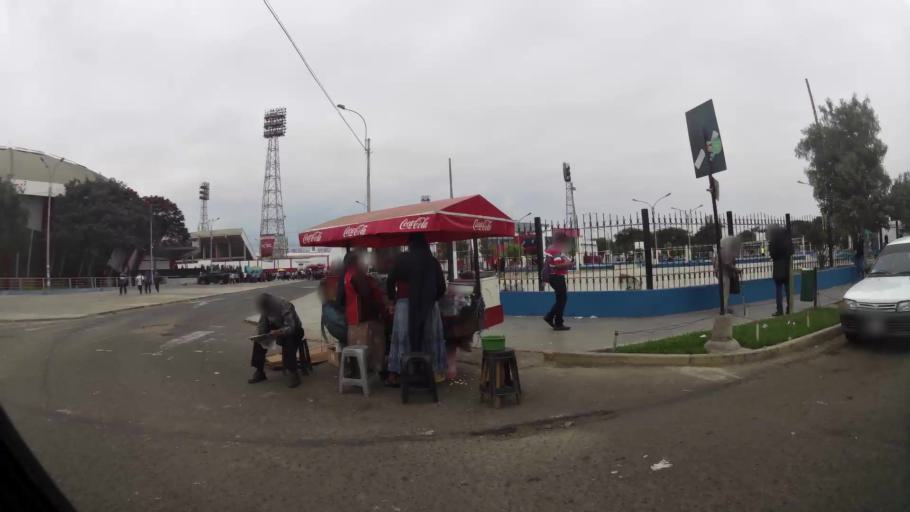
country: PE
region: La Libertad
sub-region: Provincia de Trujillo
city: Trujillo
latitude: -8.1052
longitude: -79.0322
